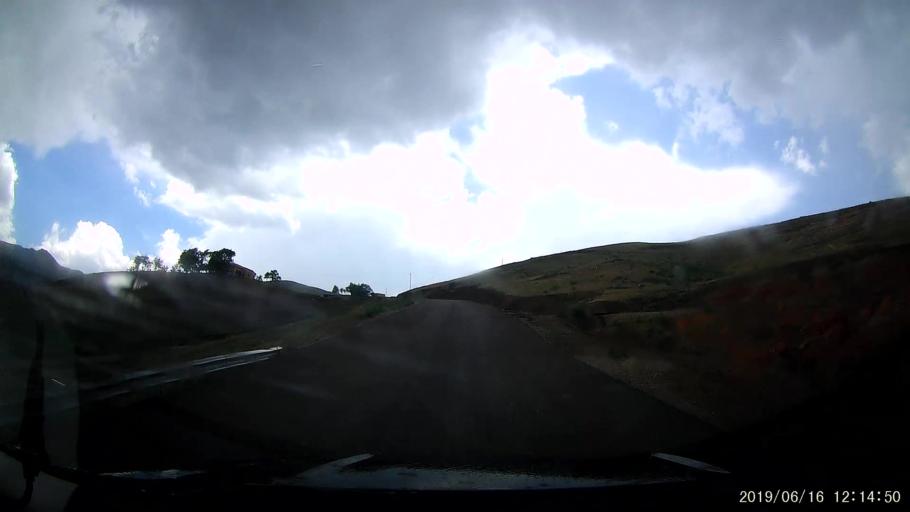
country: TR
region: Agri
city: Dogubayazit
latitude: 39.4441
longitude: 44.2348
